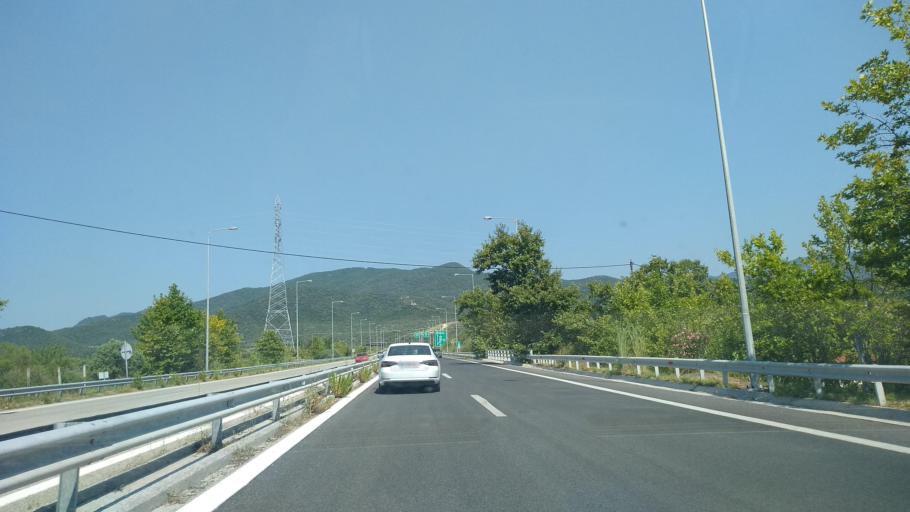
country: GR
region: Central Macedonia
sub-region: Nomos Thessalonikis
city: Nea Vrasna
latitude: 40.7065
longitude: 23.6887
